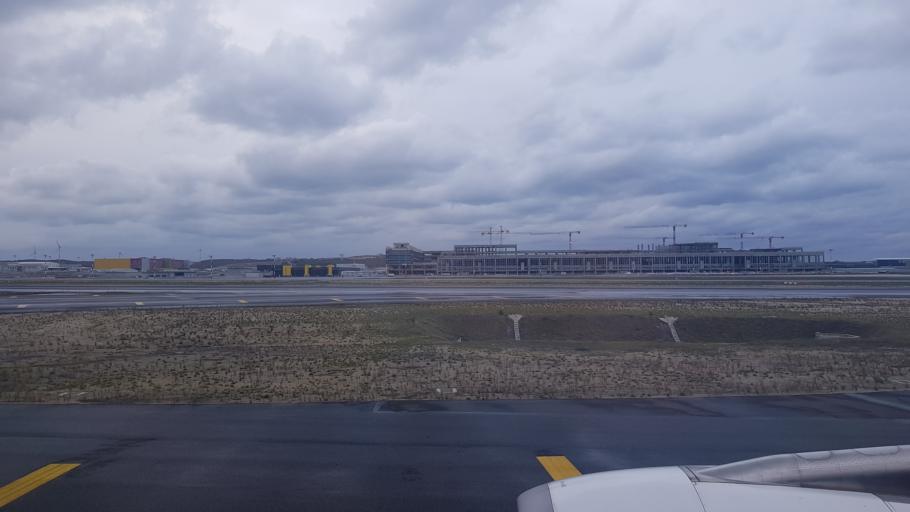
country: TR
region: Istanbul
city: Durusu
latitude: 41.2757
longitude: 28.7296
